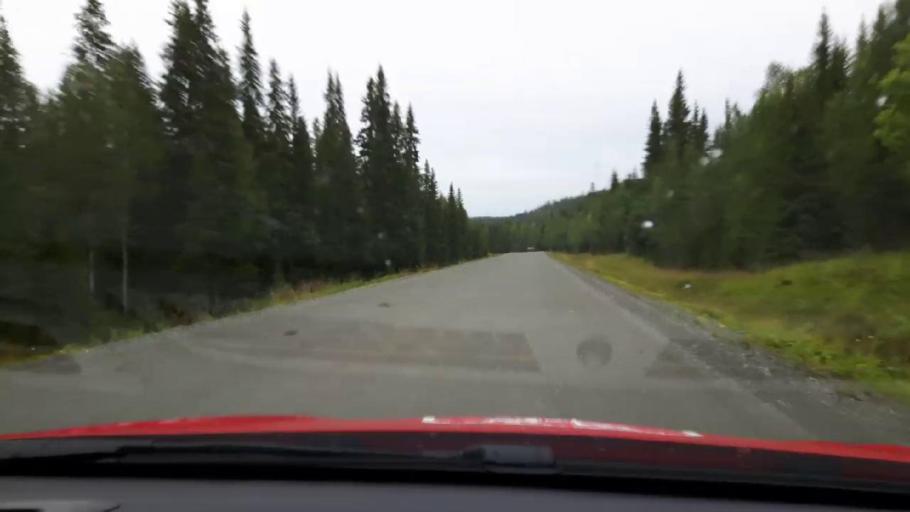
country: SE
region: Jaemtland
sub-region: Are Kommun
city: Are
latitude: 63.4186
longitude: 12.7563
